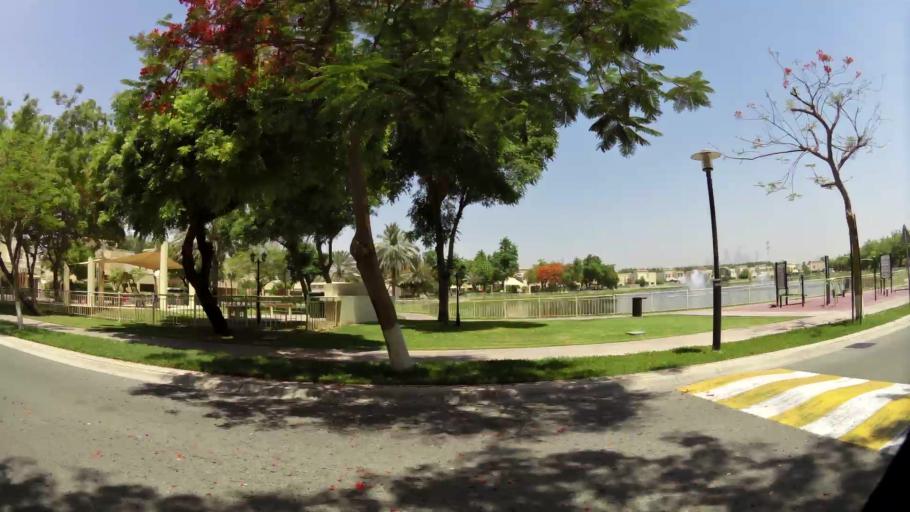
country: AE
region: Dubai
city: Dubai
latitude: 25.0442
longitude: 55.1742
